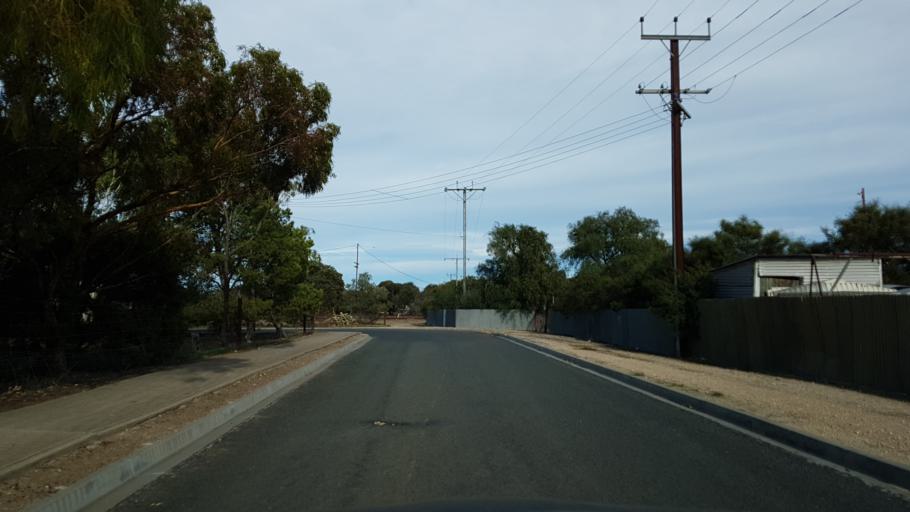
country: AU
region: South Australia
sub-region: Murray Bridge
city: Tailem Bend
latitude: -35.2508
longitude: 139.4537
